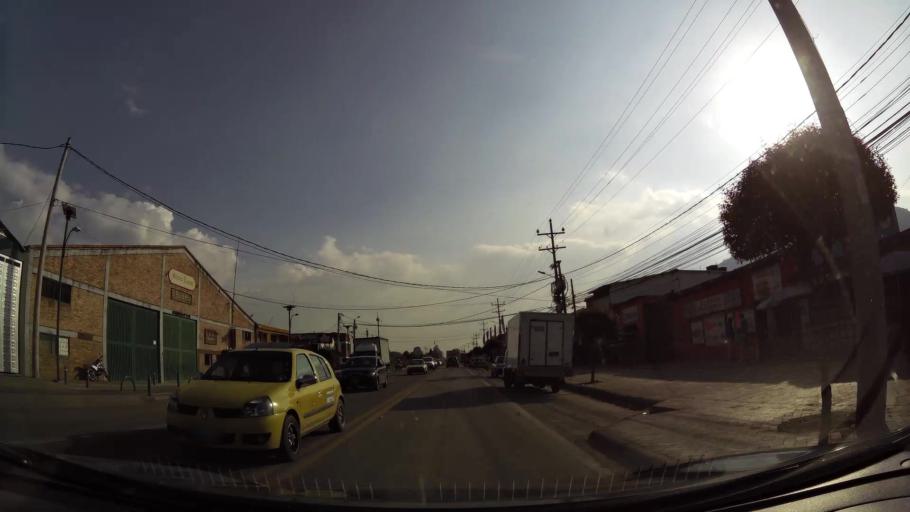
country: CO
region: Cundinamarca
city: Cota
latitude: 4.8045
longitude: -74.1065
